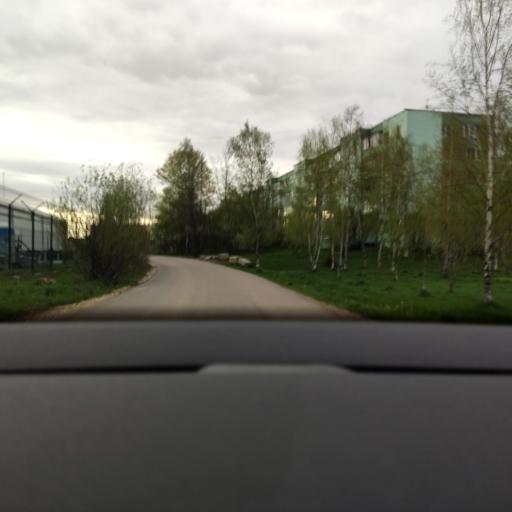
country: RU
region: Moskovskaya
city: Novopodrezkovo
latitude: 55.9909
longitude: 37.3362
